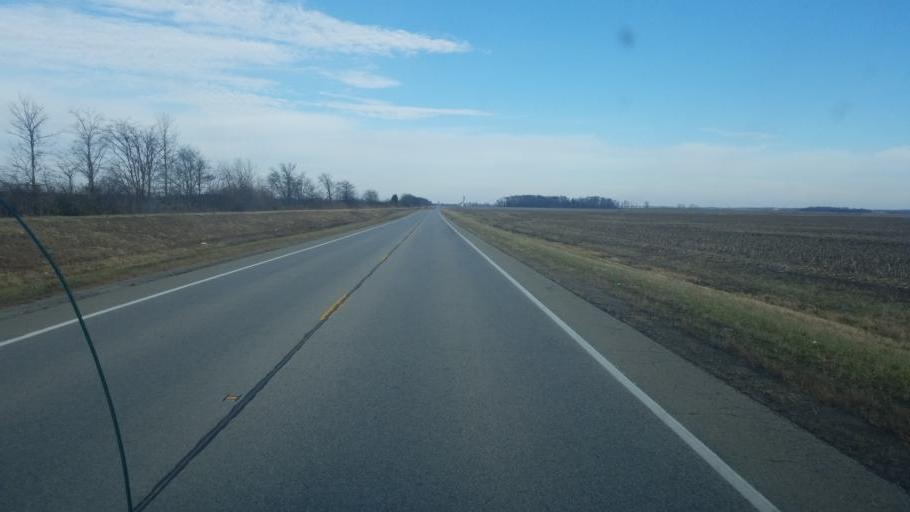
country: US
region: Illinois
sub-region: White County
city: Carmi
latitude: 38.1249
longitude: -88.1060
